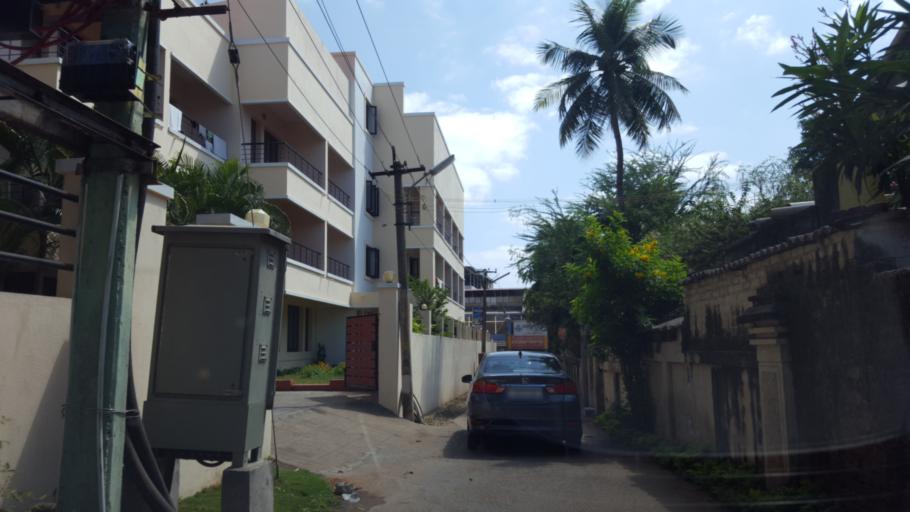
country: IN
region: Tamil Nadu
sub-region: Kancheepuram
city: Mamallapuram
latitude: 12.6180
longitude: 80.1944
